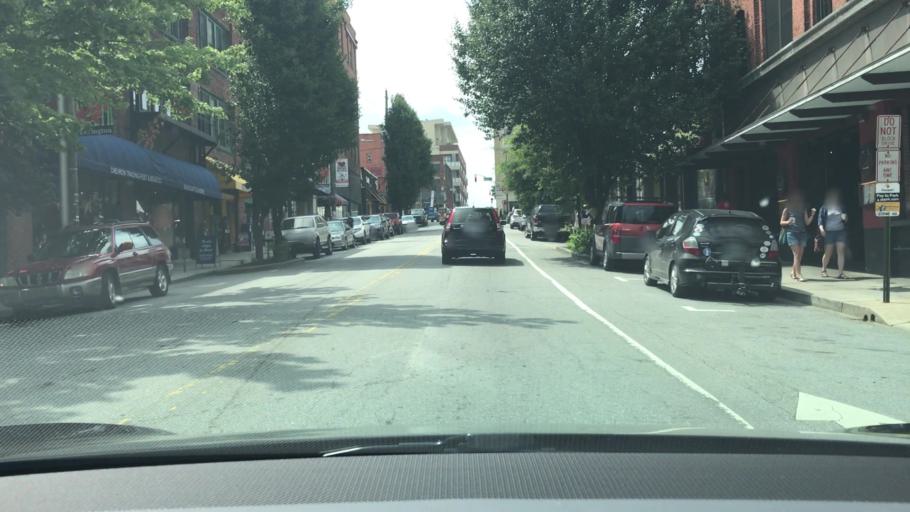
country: US
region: North Carolina
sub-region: Buncombe County
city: Asheville
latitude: 35.5964
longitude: -82.5532
